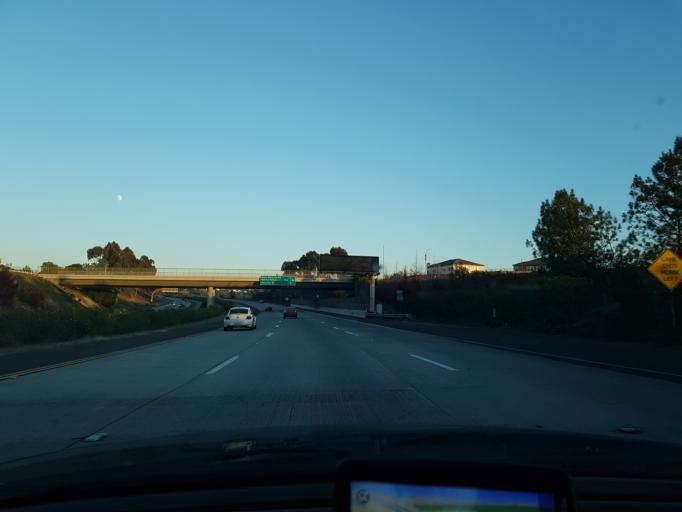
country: US
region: California
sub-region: San Diego County
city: Fairbanks Ranch
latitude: 32.9554
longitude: -117.1487
